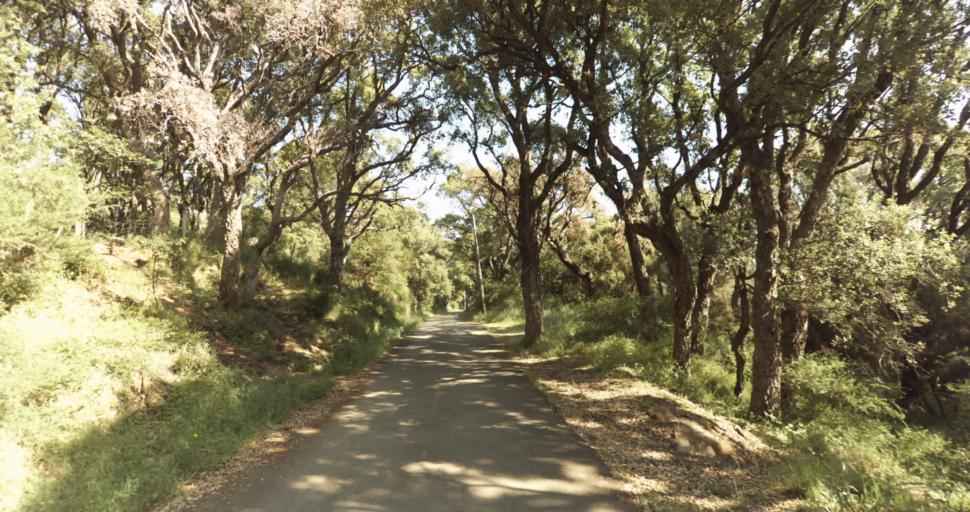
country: FR
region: Corsica
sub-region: Departement de la Haute-Corse
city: Biguglia
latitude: 42.6372
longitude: 9.4168
